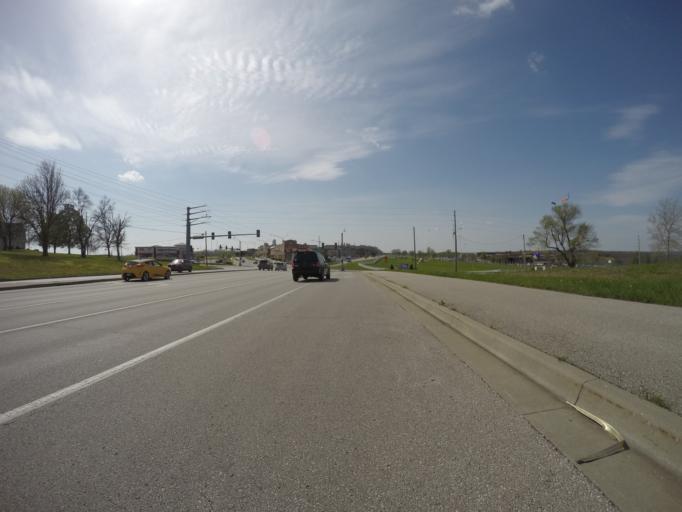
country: US
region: Missouri
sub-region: Jackson County
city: Lees Summit
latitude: 38.9139
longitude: -94.4511
